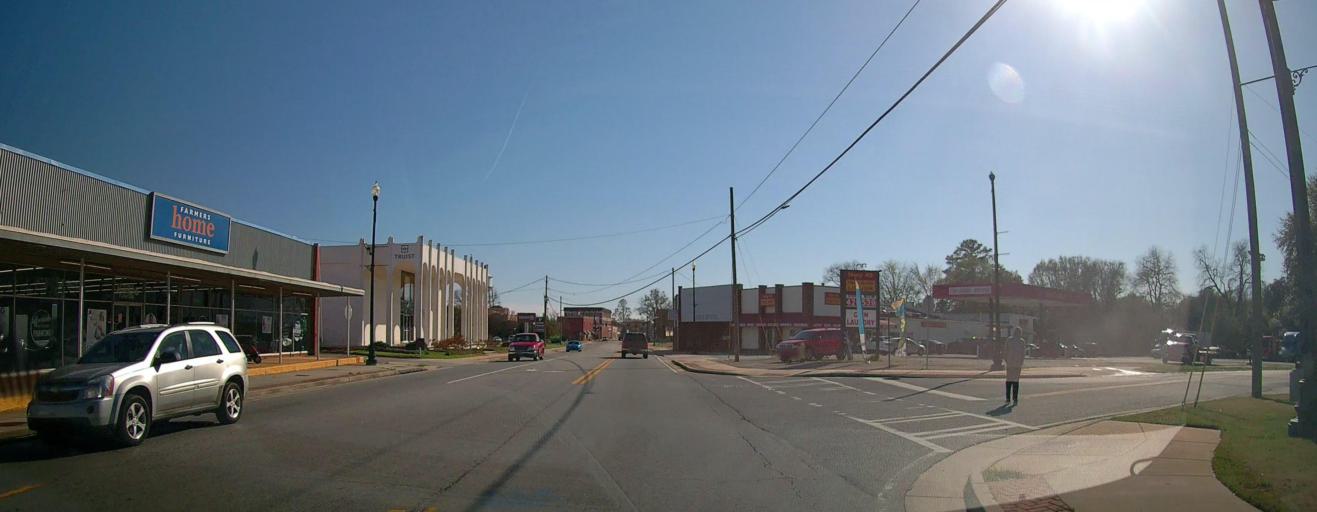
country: US
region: Georgia
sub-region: Peach County
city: Fort Valley
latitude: 32.5561
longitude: -83.8851
